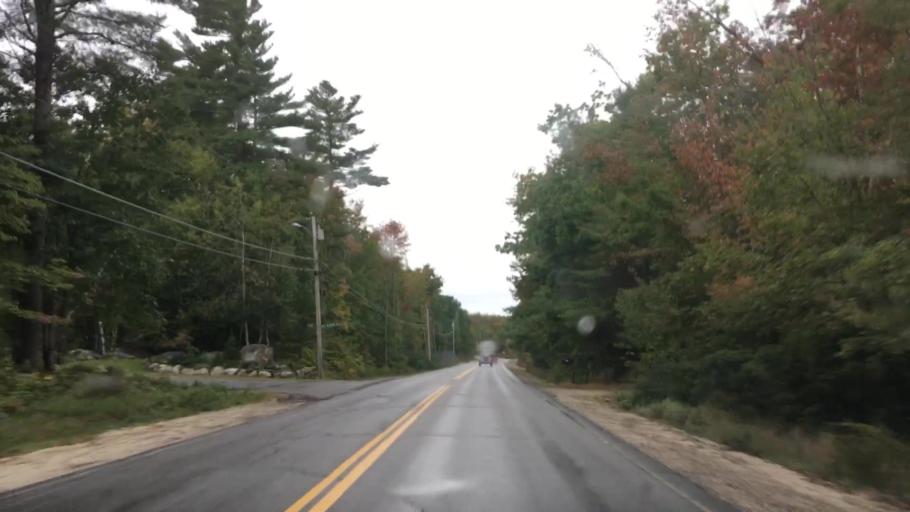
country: US
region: Maine
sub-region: Cumberland County
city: Raymond
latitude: 43.9280
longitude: -70.3776
